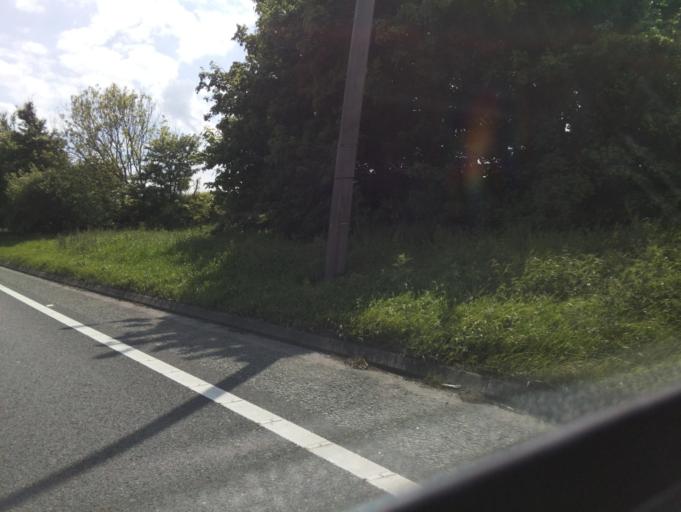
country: GB
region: England
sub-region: County Durham
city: Peterlee
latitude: 54.7192
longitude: -1.3284
